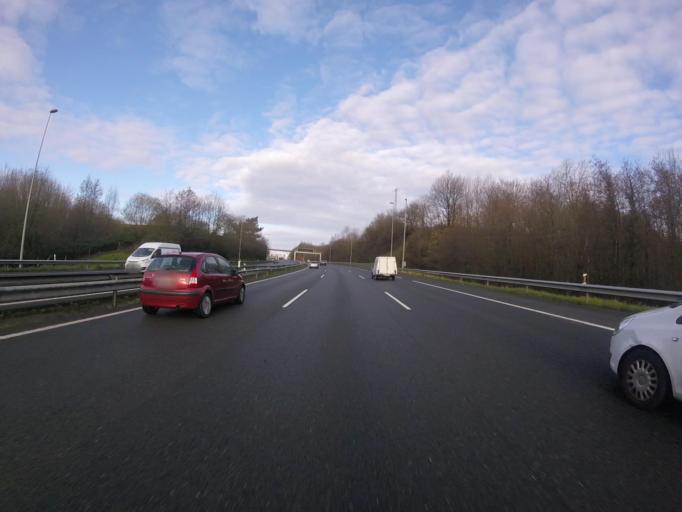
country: ES
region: Basque Country
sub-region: Provincia de Guipuzcoa
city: Pasaia
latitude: 43.3100
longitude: -1.9316
